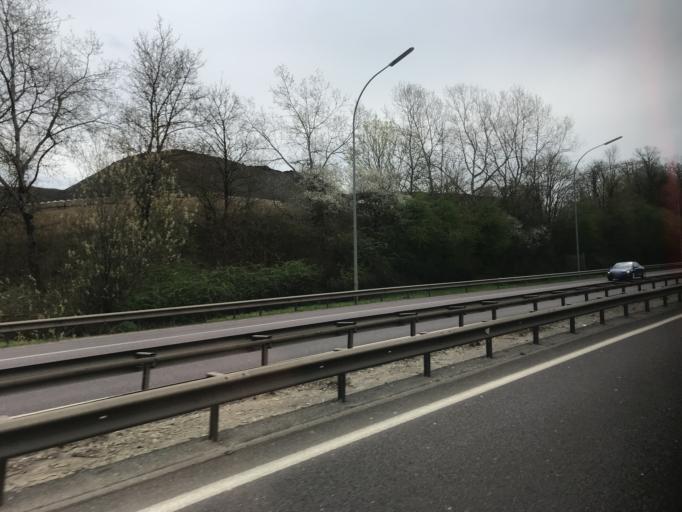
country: LU
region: Luxembourg
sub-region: Canton d'Esch-sur-Alzette
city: Leudelange
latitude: 49.5774
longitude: 6.0882
